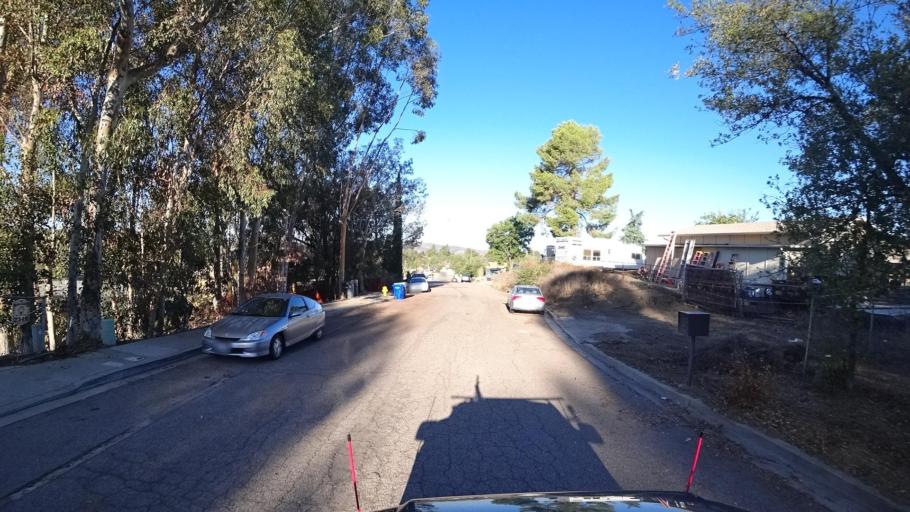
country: US
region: California
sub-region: San Diego County
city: Alpine
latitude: 32.8334
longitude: -116.7641
